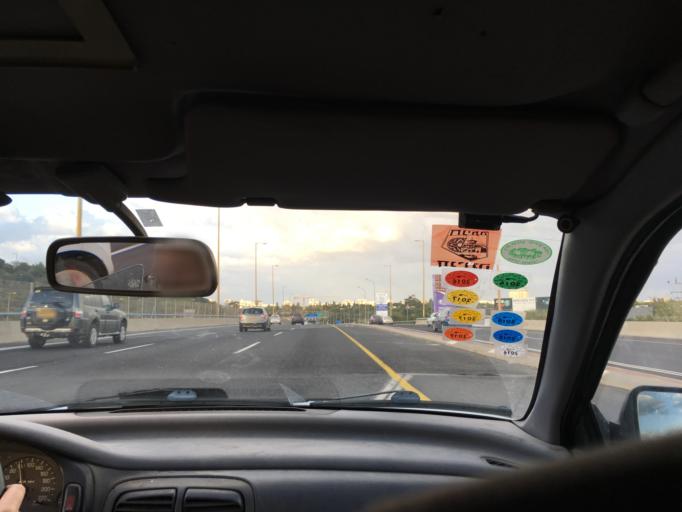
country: IL
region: Tel Aviv
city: Ramat Gan
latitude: 32.1061
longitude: 34.8066
